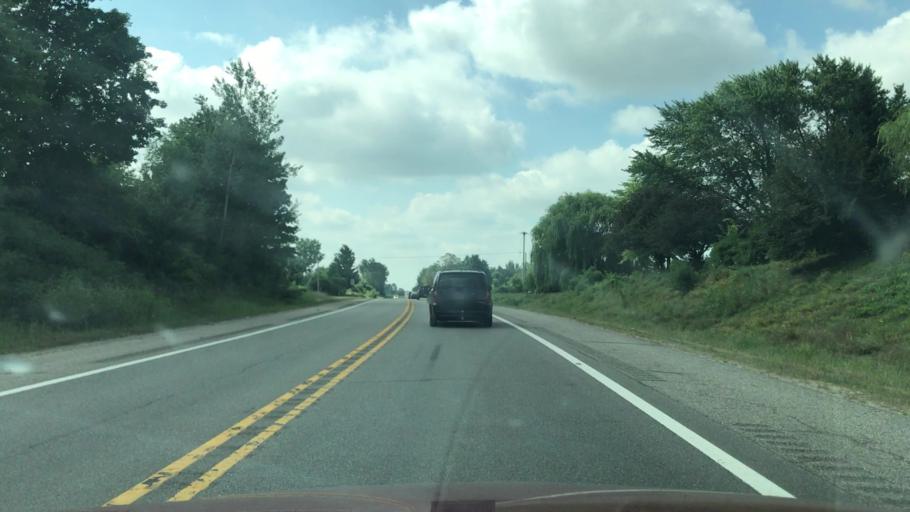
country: US
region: Michigan
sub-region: Kent County
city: Kent City
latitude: 43.2578
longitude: -85.8145
